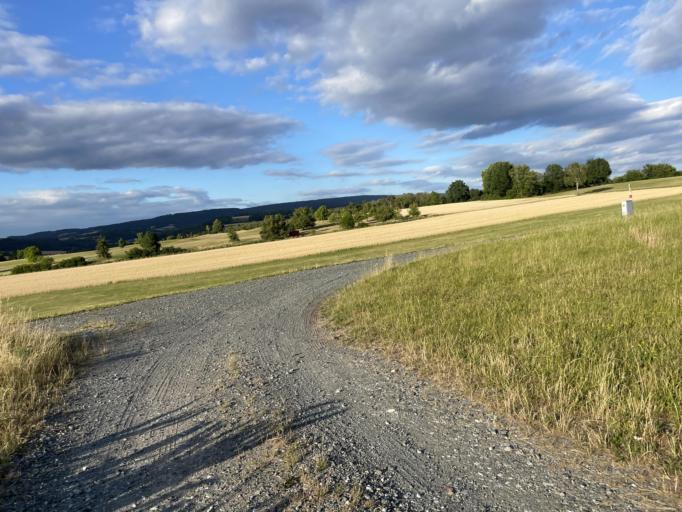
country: DE
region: Bavaria
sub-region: Upper Franconia
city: Neunkirchen am Main
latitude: 49.9492
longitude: 11.6454
